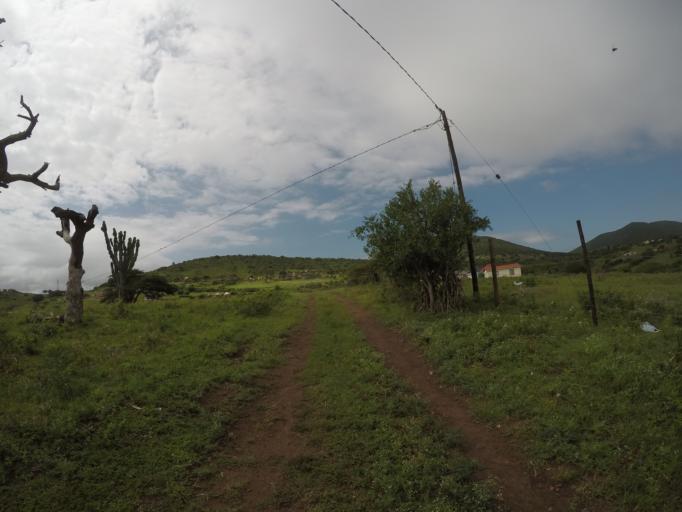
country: ZA
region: KwaZulu-Natal
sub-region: uThungulu District Municipality
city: Empangeni
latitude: -28.6268
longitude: 31.8634
